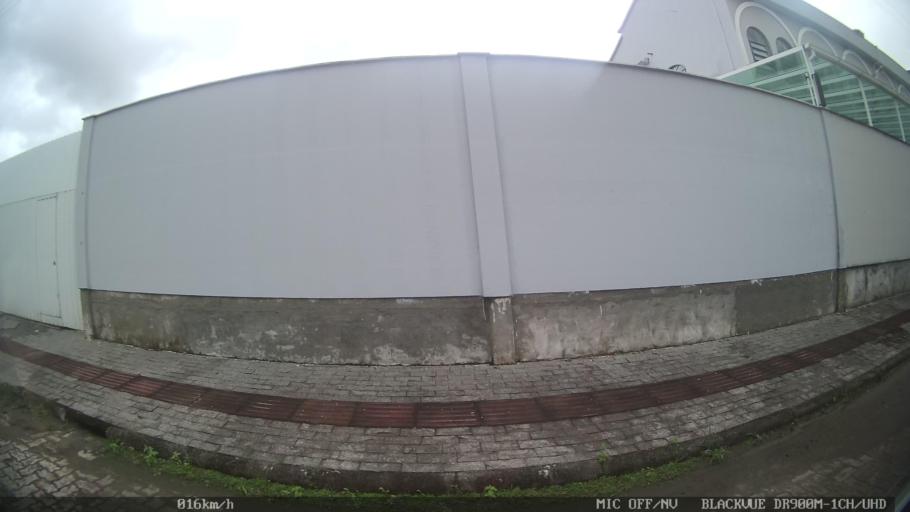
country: BR
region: Santa Catarina
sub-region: Biguacu
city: Biguacu
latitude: -27.5055
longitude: -48.6534
